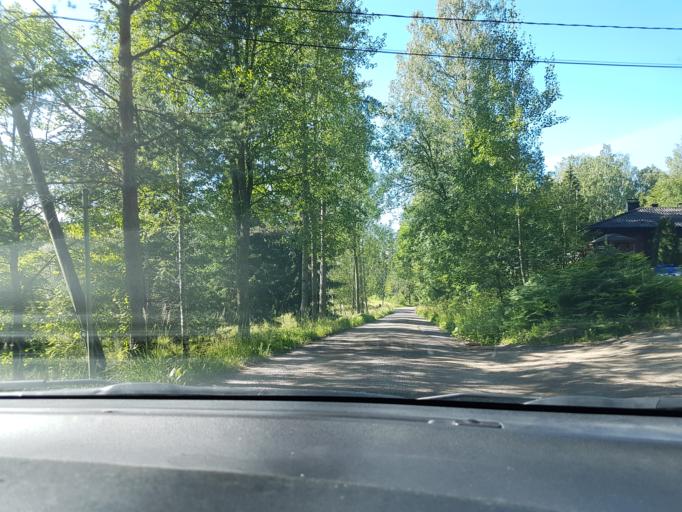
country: FI
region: Uusimaa
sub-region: Helsinki
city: Sibbo
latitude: 60.2898
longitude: 25.2404
